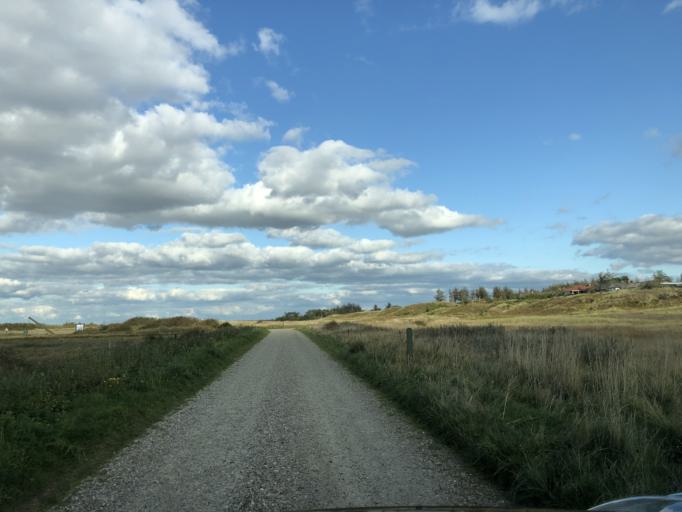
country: DK
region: Central Jutland
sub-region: Holstebro Kommune
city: Ulfborg
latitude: 56.3292
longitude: 8.1471
